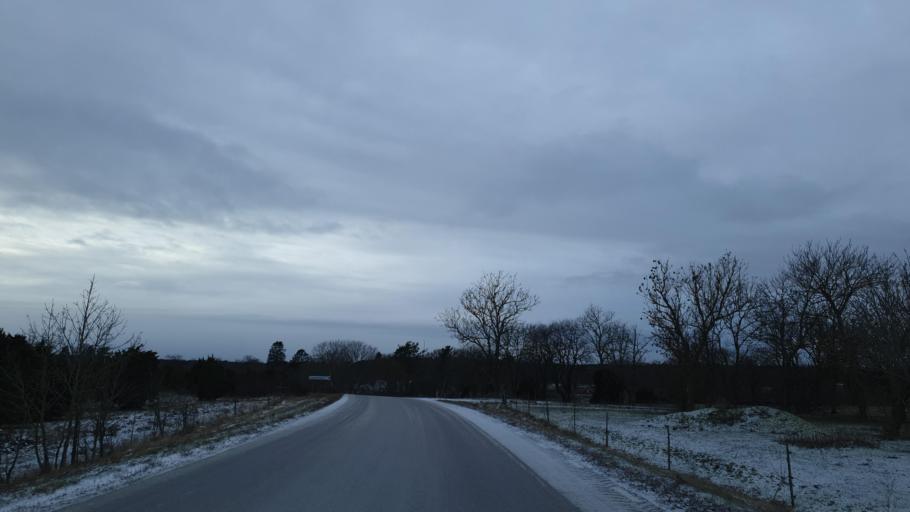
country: SE
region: Gotland
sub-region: Gotland
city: Slite
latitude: 57.4192
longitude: 18.8816
